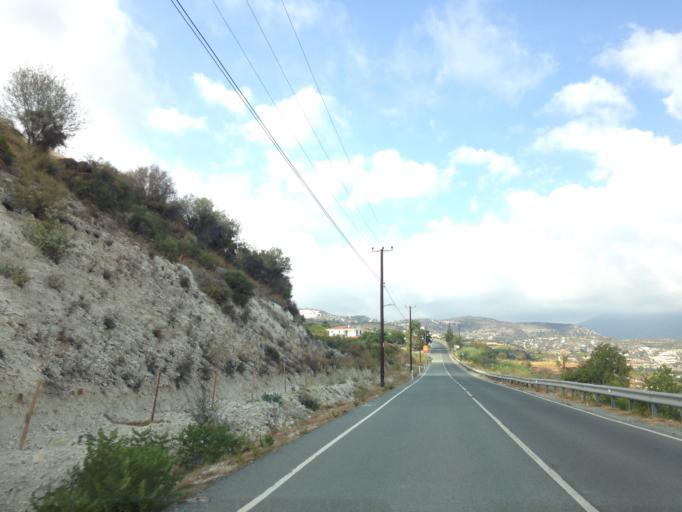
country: CY
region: Limassol
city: Pachna
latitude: 34.8402
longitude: 32.8082
